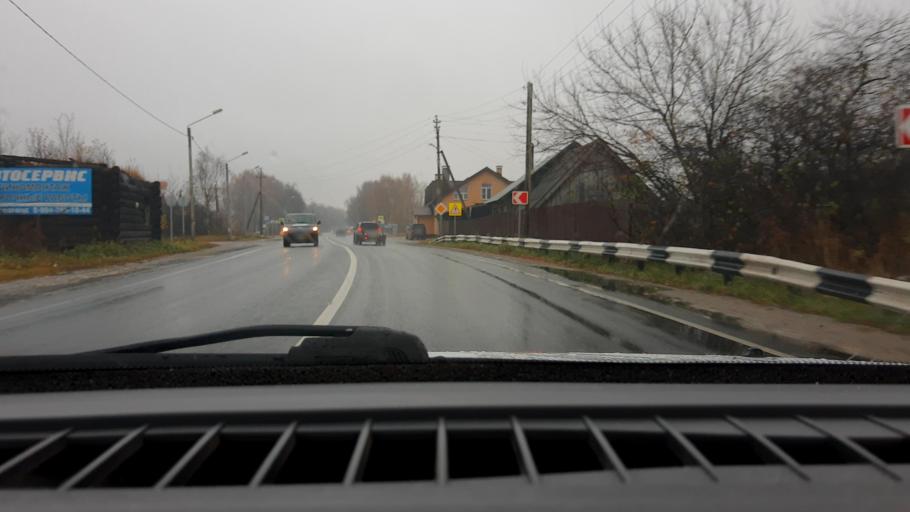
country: RU
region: Nizjnij Novgorod
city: Sitniki
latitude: 56.5443
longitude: 44.0188
